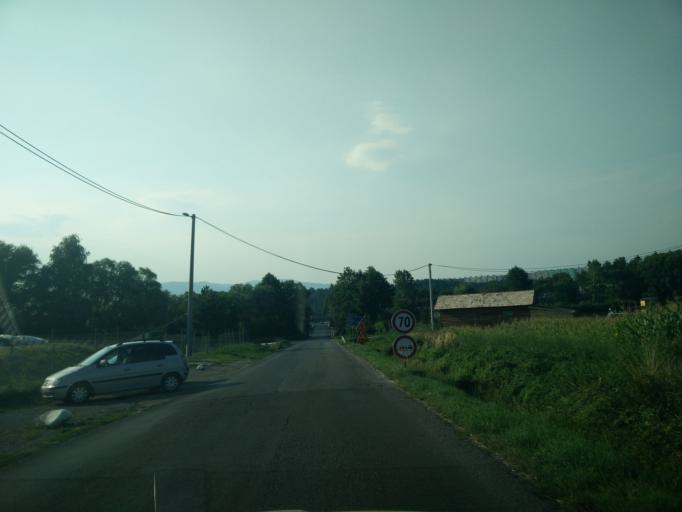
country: SK
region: Nitriansky
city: Prievidza
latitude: 48.7662
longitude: 18.6497
